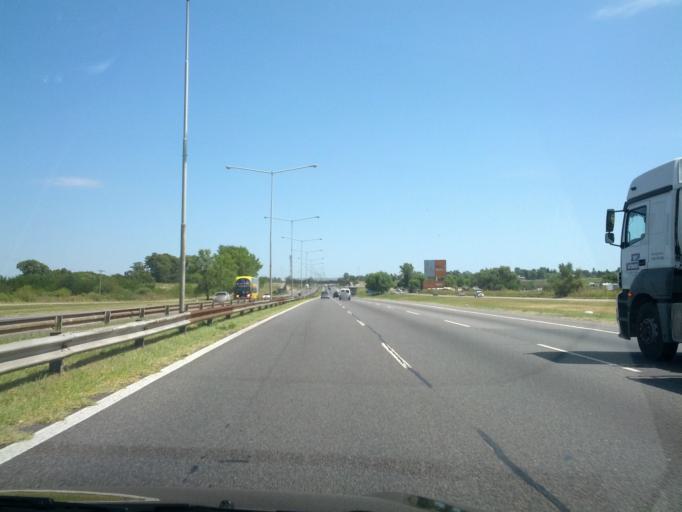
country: AR
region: Buenos Aires
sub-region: Partido de Campana
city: Campana
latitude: -34.2336
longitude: -58.9131
